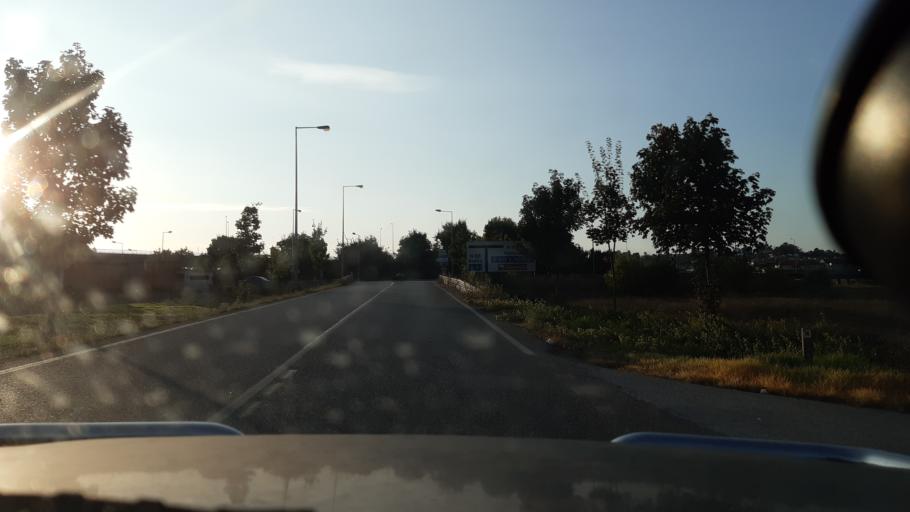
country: PT
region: Aveiro
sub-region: Agueda
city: Agueda
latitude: 40.5660
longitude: -8.4469
